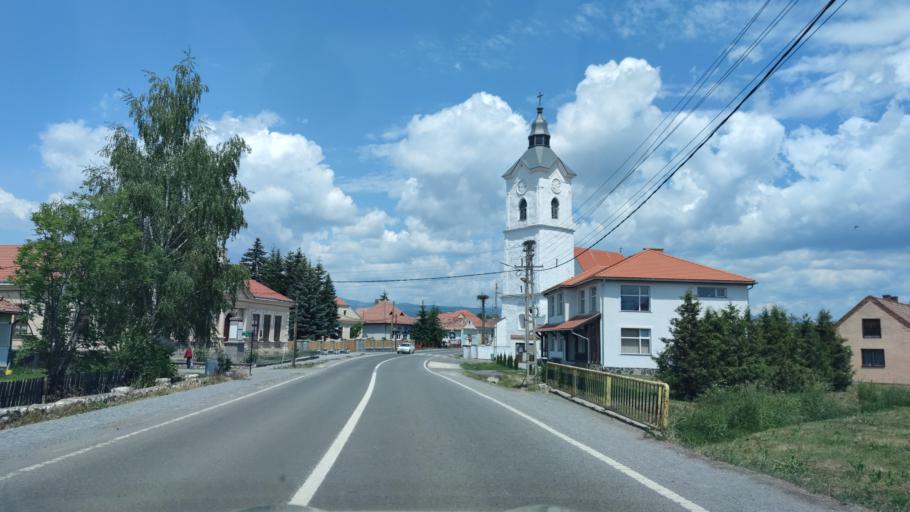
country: RO
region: Harghita
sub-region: Comuna Suseni
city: Valea Stramba
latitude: 46.6932
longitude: 25.5967
